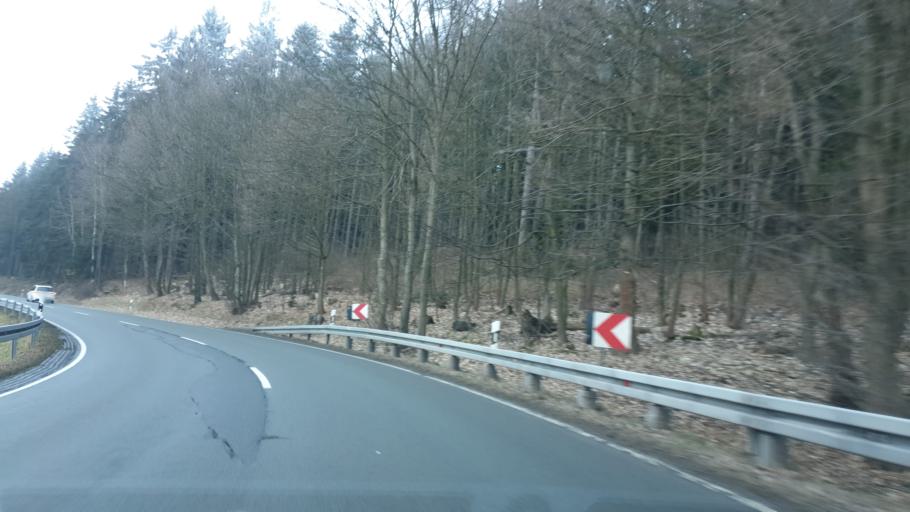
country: DE
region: Saxony
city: Bad Brambach
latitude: 50.2371
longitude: 12.3059
